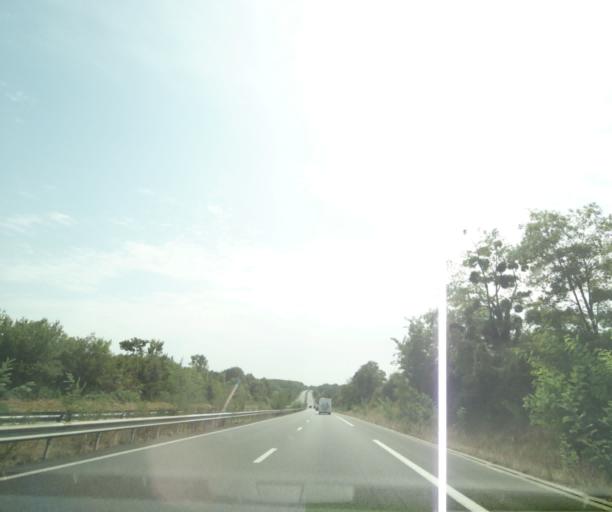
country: FR
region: Poitou-Charentes
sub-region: Departement de la Charente-Maritime
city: Saint-Savinien
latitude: 45.8720
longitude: -0.6229
